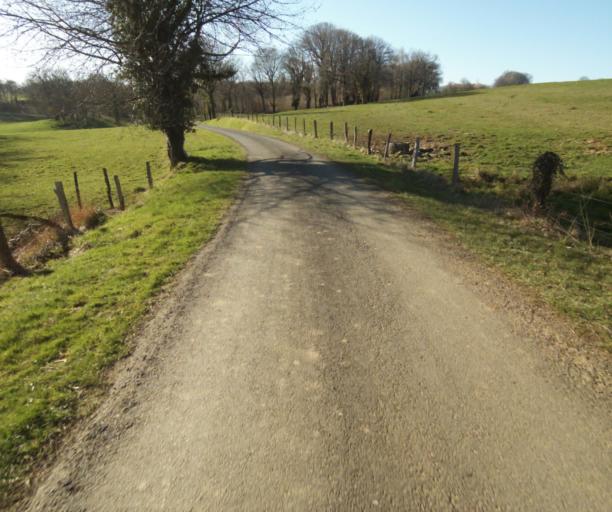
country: FR
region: Limousin
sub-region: Departement de la Correze
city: Seilhac
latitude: 45.3858
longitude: 1.6949
